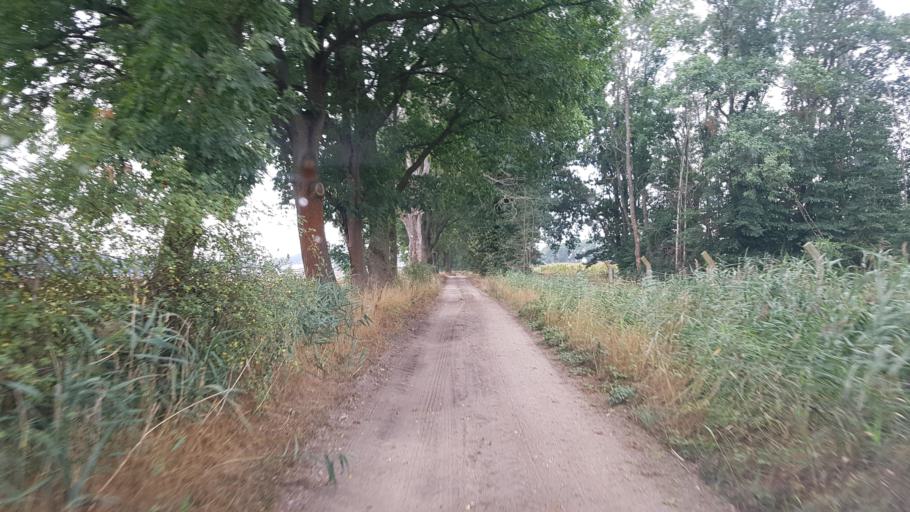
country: DE
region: Brandenburg
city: Bronkow
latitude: 51.6195
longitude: 13.9104
